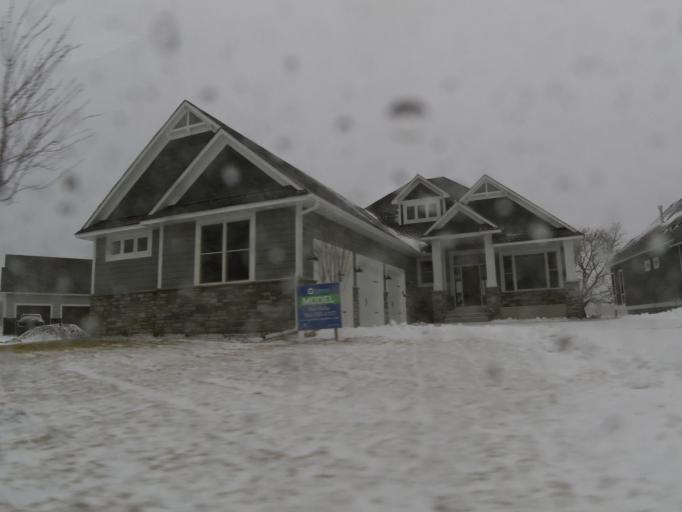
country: US
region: Minnesota
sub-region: Washington County
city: Lake Elmo
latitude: 44.9757
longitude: -92.8669
